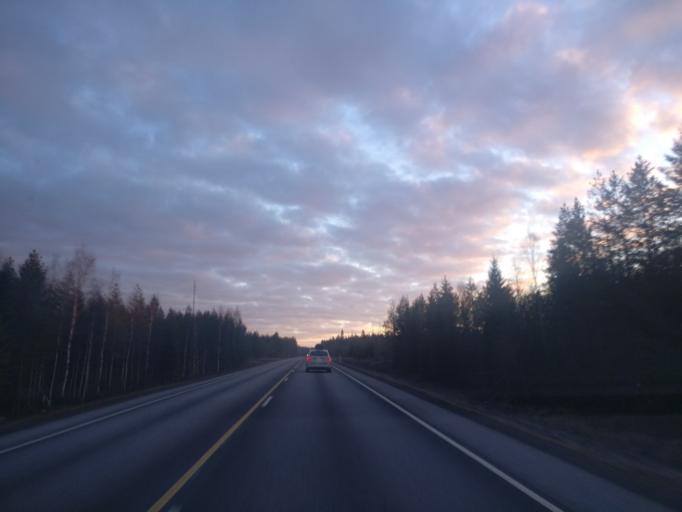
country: FI
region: Northern Ostrobothnia
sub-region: Haapavesi-Siikalatva
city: Pulkkila
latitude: 64.2303
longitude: 25.8402
